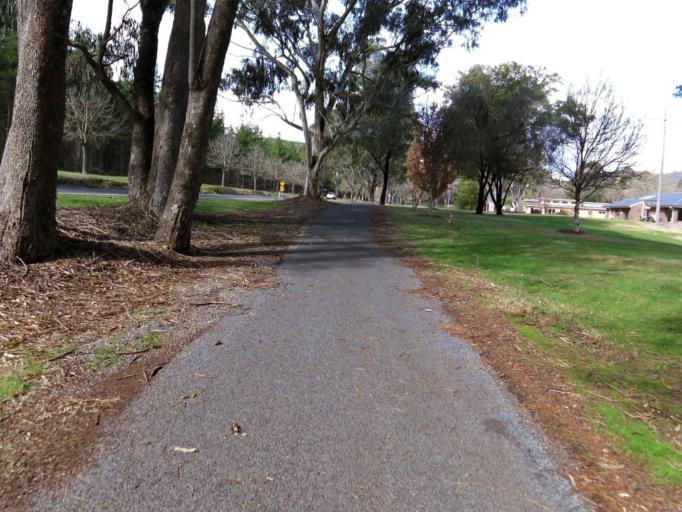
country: AU
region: Victoria
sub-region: Alpine
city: Mount Beauty
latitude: -36.7138
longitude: 146.9400
